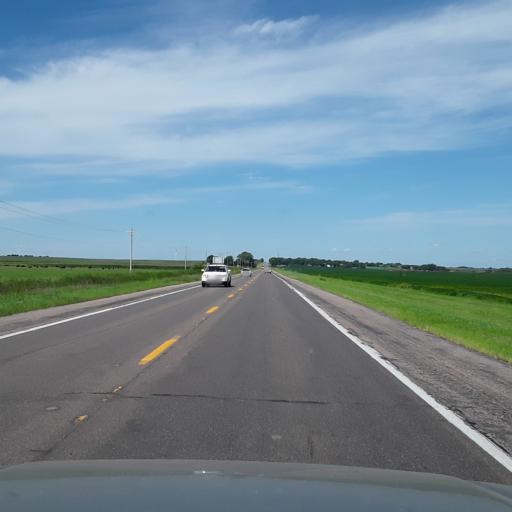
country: US
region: Nebraska
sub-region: Seward County
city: Seward
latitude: 40.9017
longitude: -97.1209
